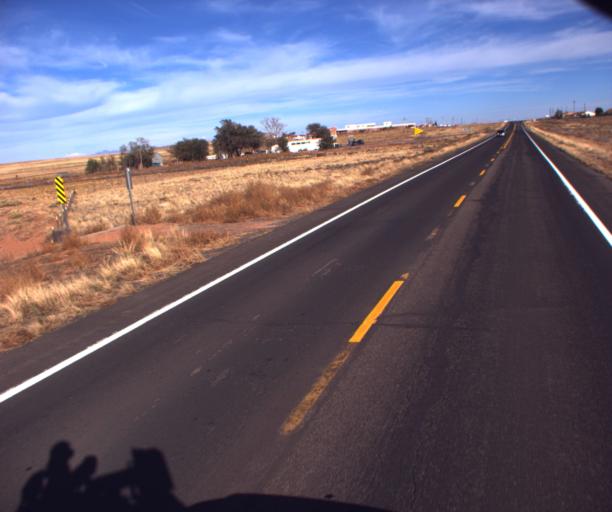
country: US
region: Arizona
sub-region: Apache County
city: Lukachukai
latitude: 36.9600
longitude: -109.3590
